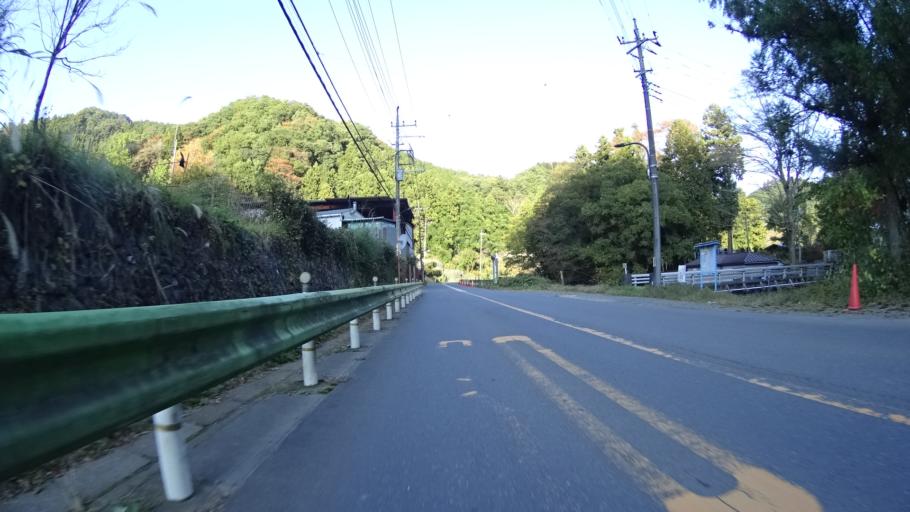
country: JP
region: Tokyo
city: Itsukaichi
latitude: 35.6718
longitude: 139.2276
